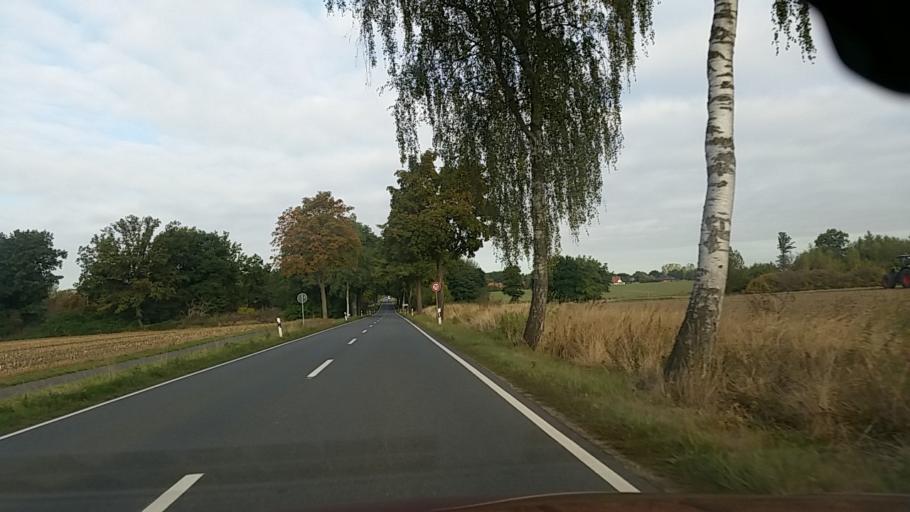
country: DE
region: Lower Saxony
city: Ahnsbeck
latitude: 52.6017
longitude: 10.3013
